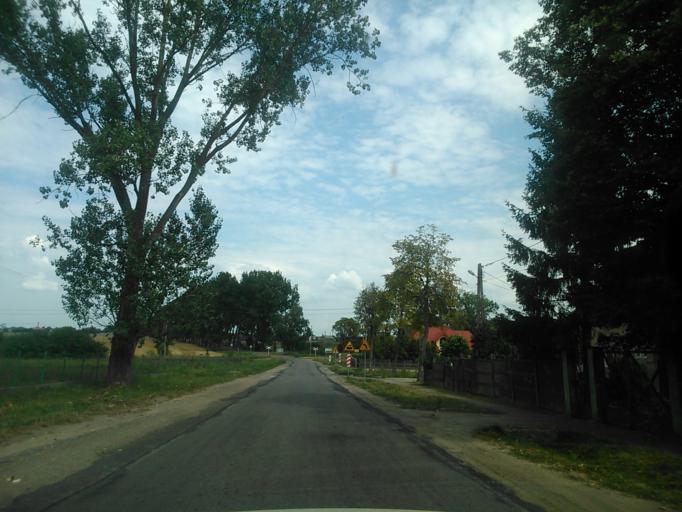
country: PL
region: Masovian Voivodeship
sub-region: Powiat ciechanowski
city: Grudusk
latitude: 53.0626
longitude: 20.6244
